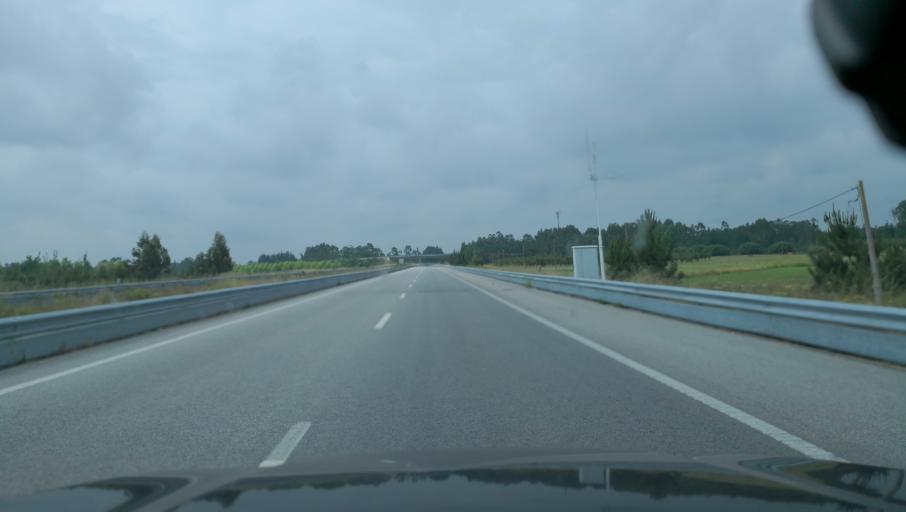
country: PT
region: Coimbra
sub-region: Figueira da Foz
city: Alhadas
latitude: 40.2633
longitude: -8.7610
